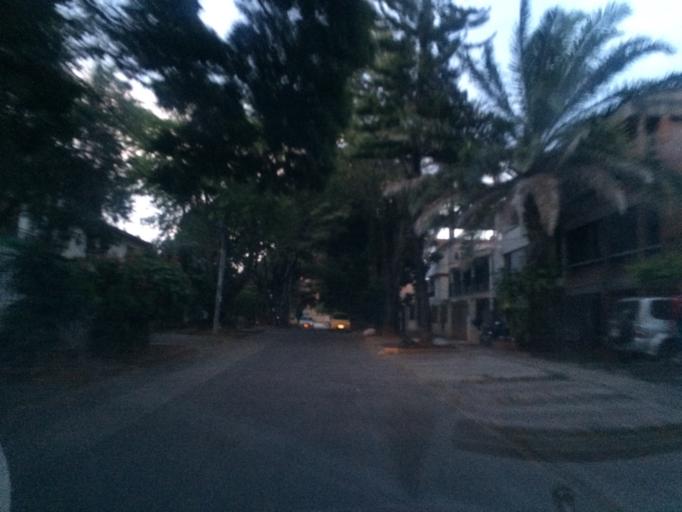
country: CO
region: Valle del Cauca
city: Cali
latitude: 3.4217
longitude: -76.5513
